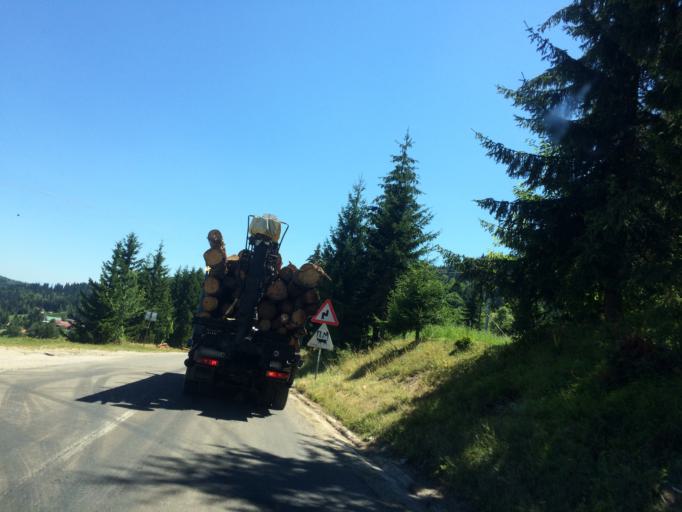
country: RS
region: Central Serbia
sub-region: Zlatiborski Okrug
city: Prijepolje
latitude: 43.3400
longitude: 19.5192
